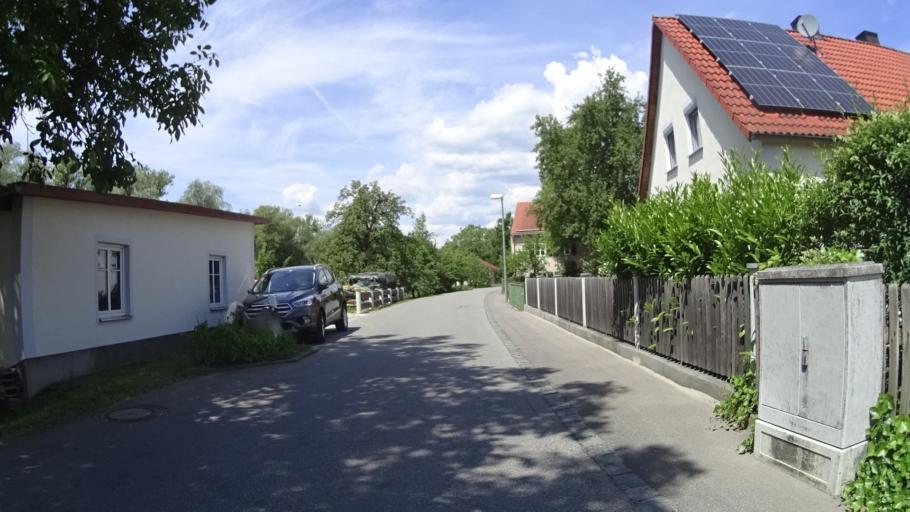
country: DE
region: Bavaria
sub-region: Lower Bavaria
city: Bad Abbach
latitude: 48.9459
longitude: 12.0219
